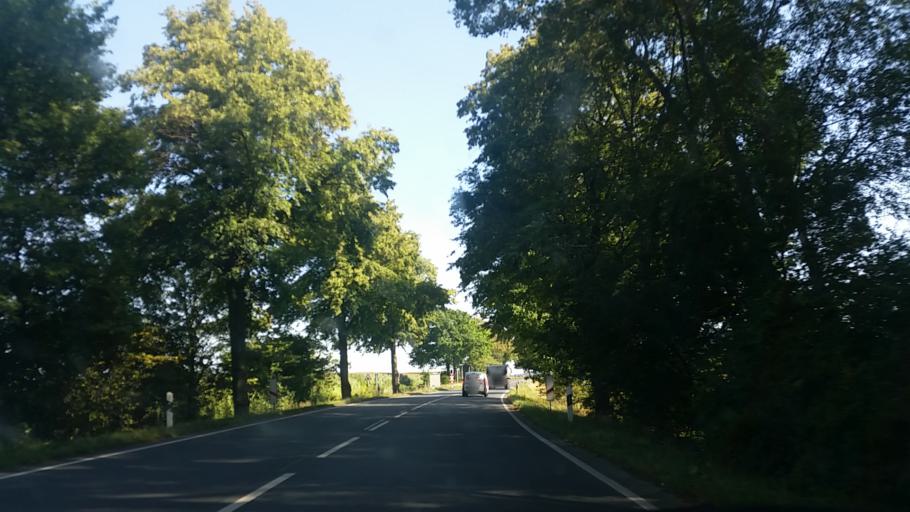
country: DE
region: Lower Saxony
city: Salzhemmendorf
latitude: 52.0977
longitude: 9.5849
